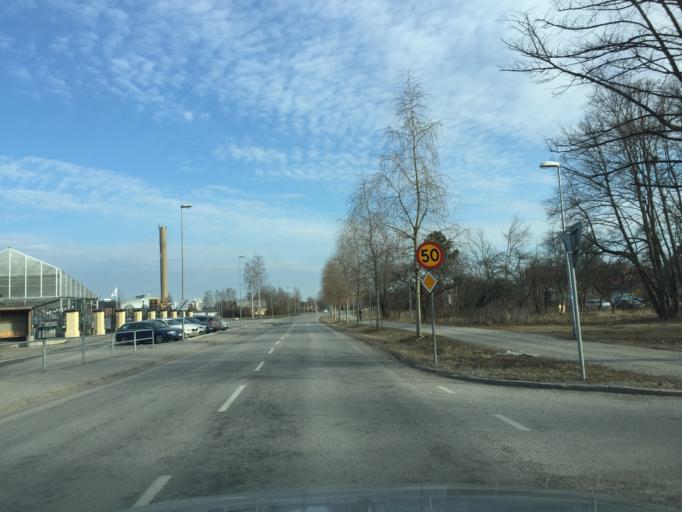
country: SE
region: OErebro
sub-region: Orebro Kommun
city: Orebro
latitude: 59.2627
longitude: 15.2393
